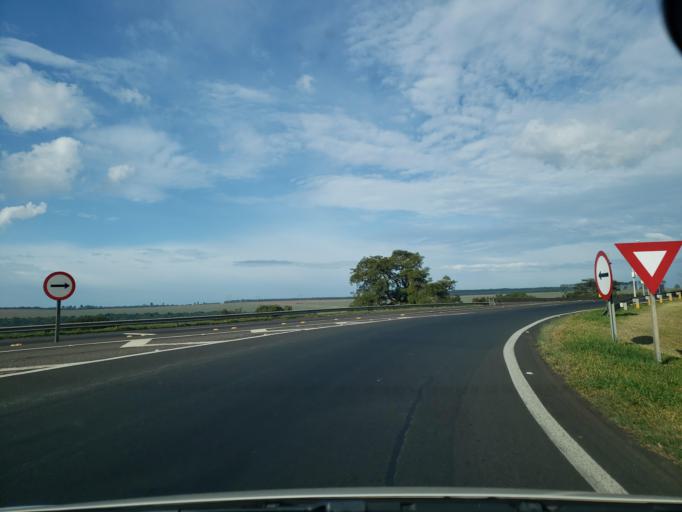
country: BR
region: Sao Paulo
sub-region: Itirapina
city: Itirapina
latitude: -22.2148
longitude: -47.7660
